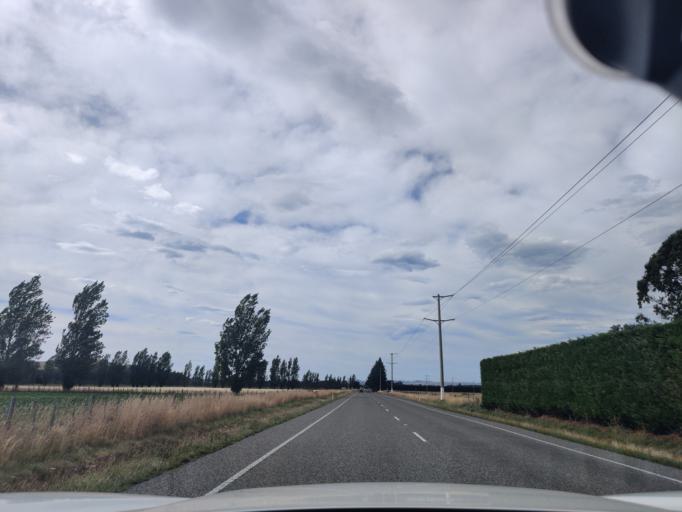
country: NZ
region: Wellington
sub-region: Masterton District
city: Masterton
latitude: -40.8501
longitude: 175.6357
